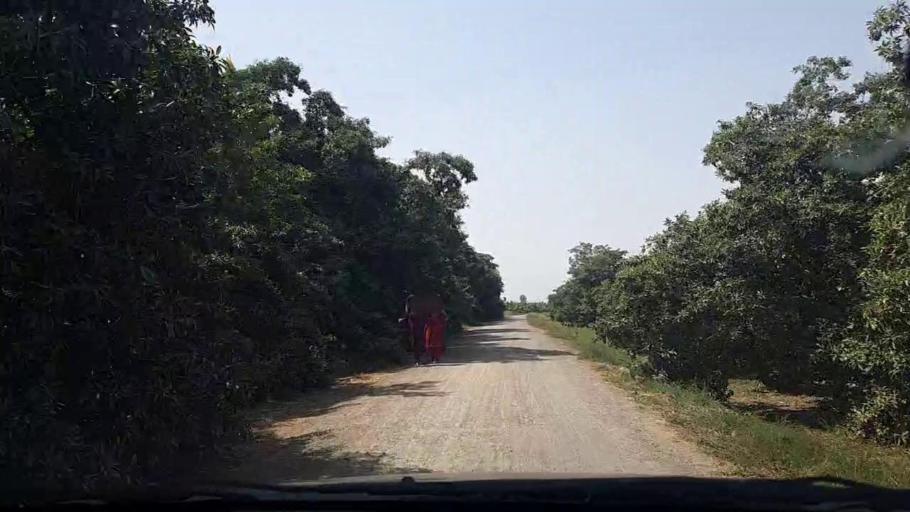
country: PK
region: Sindh
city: Keti Bandar
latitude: 24.2828
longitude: 67.6710
